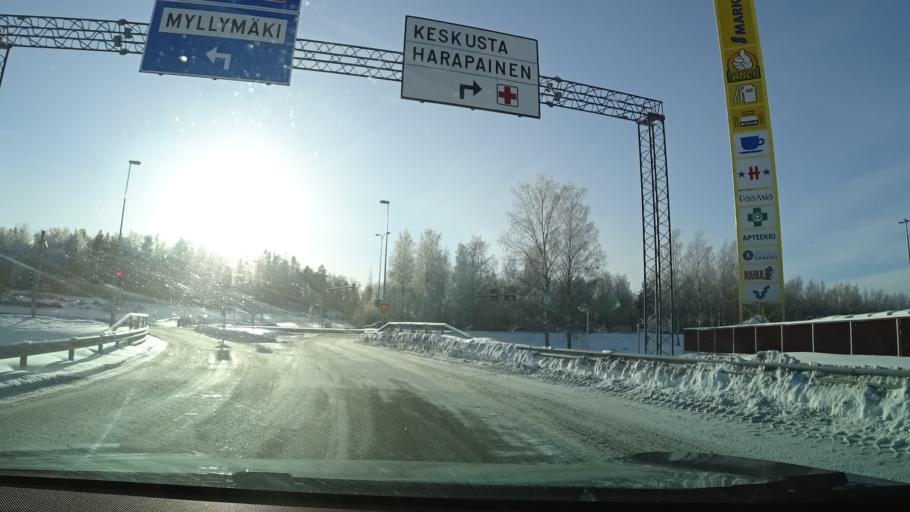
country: FI
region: South Karelia
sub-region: Lappeenranta
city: Lappeenranta
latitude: 61.0456
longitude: 28.2094
